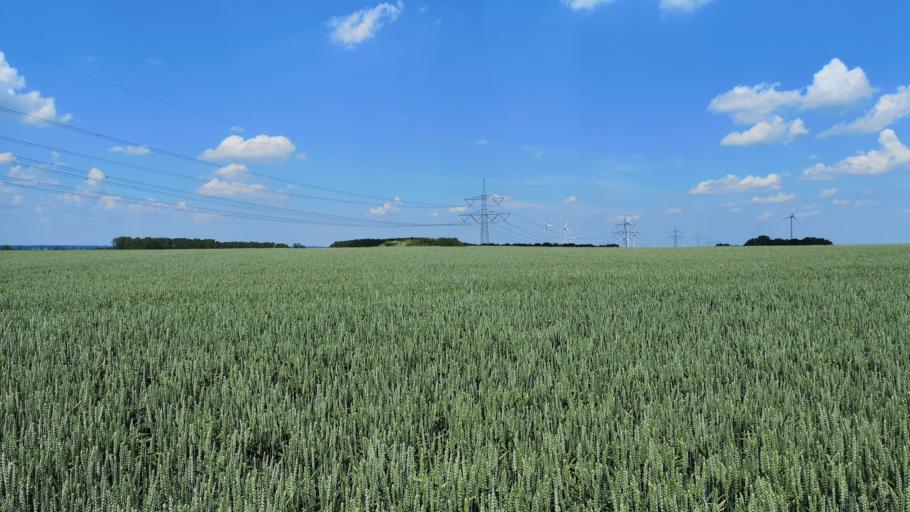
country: DE
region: Saxony-Anhalt
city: Grossorner
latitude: 51.6431
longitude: 11.4493
